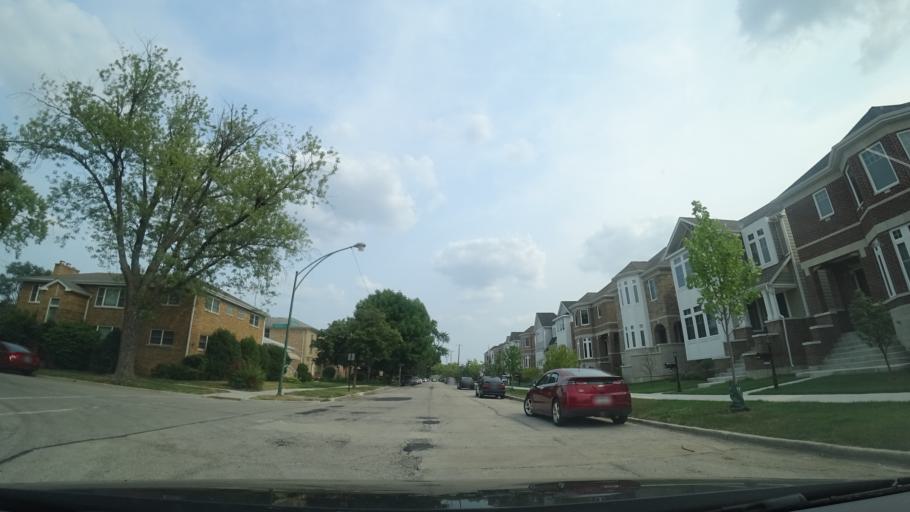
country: US
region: Illinois
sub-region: Cook County
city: Lincolnwood
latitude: 41.9918
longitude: -87.7366
